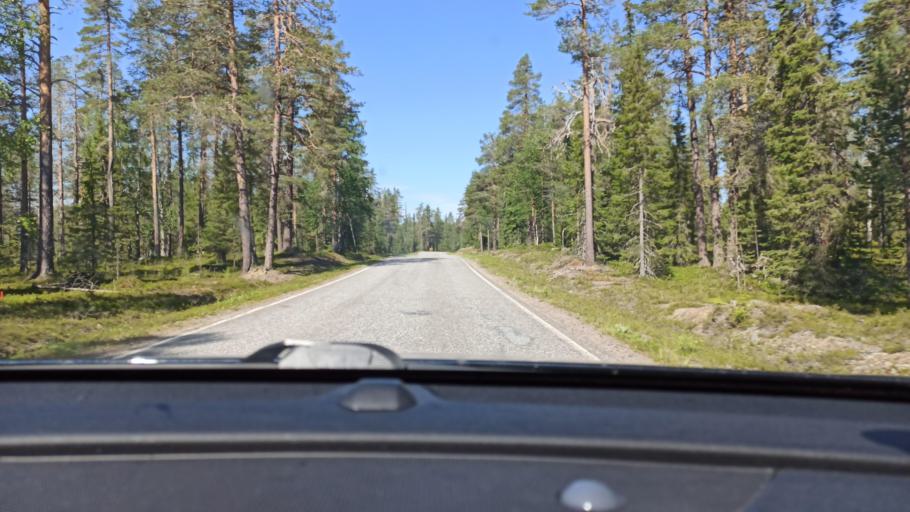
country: FI
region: Lapland
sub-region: Tunturi-Lappi
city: Kolari
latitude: 67.6697
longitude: 24.1547
